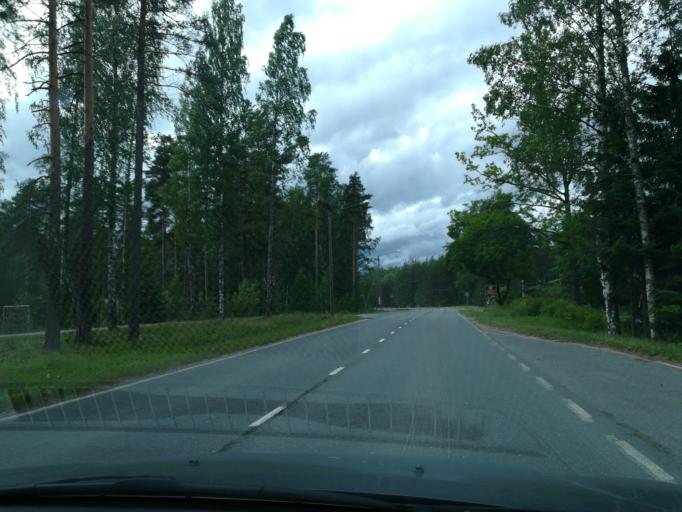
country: FI
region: South Karelia
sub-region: Lappeenranta
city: Savitaipale
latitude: 61.1967
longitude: 27.6991
